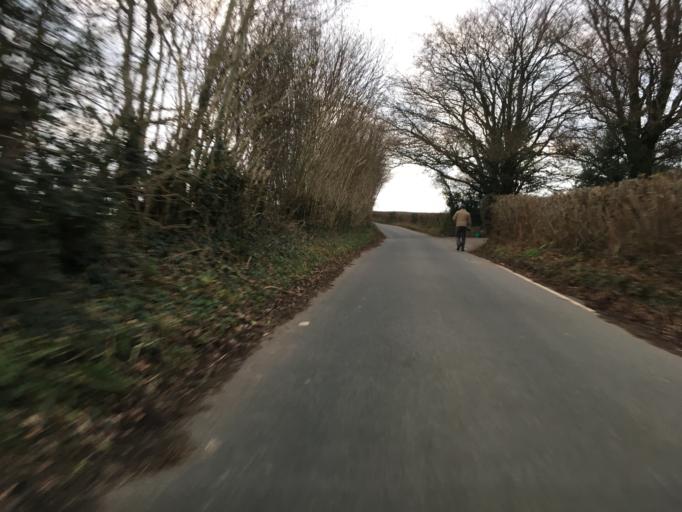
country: GB
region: Wales
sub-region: Newport
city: Marshfield
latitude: 51.5735
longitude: -3.0686
